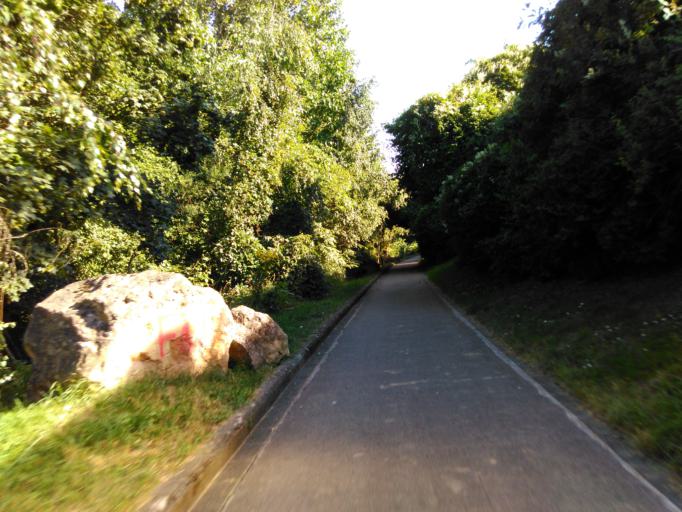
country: LU
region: Luxembourg
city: Belvaux
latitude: 49.5130
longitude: 5.9294
